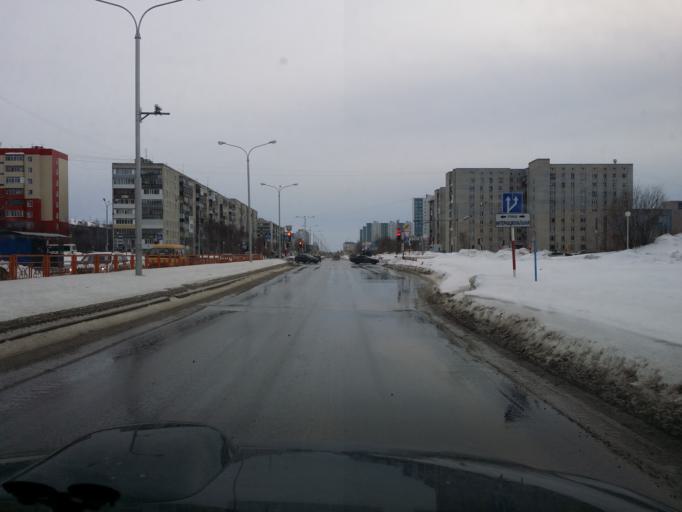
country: RU
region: Khanty-Mansiyskiy Avtonomnyy Okrug
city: Nizhnevartovsk
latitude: 60.9460
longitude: 76.6024
